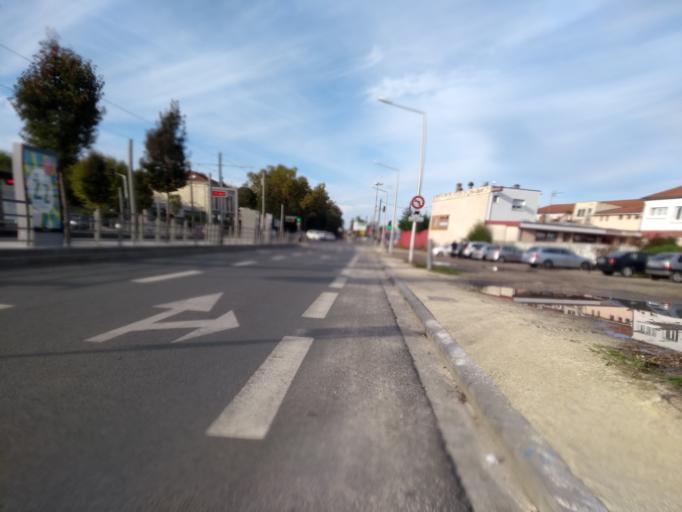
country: FR
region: Aquitaine
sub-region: Departement de la Gironde
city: Pessac
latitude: 44.7985
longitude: -0.6629
